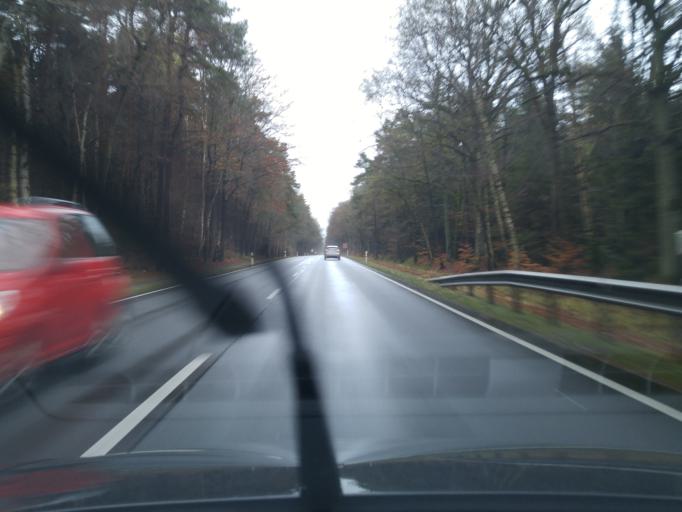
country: DE
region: Lower Saxony
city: Suderburg
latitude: 52.8799
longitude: 10.5009
